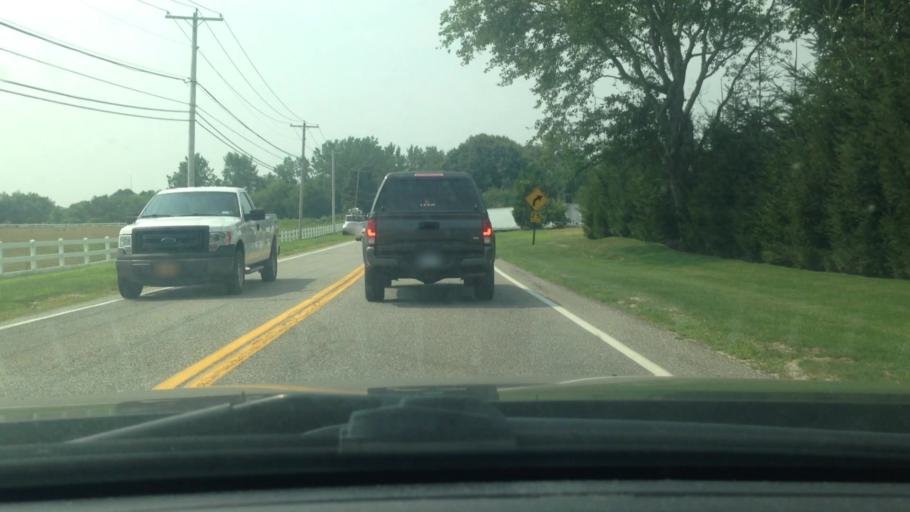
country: US
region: New York
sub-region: Suffolk County
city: Bridgehampton
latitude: 40.9476
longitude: -72.3298
